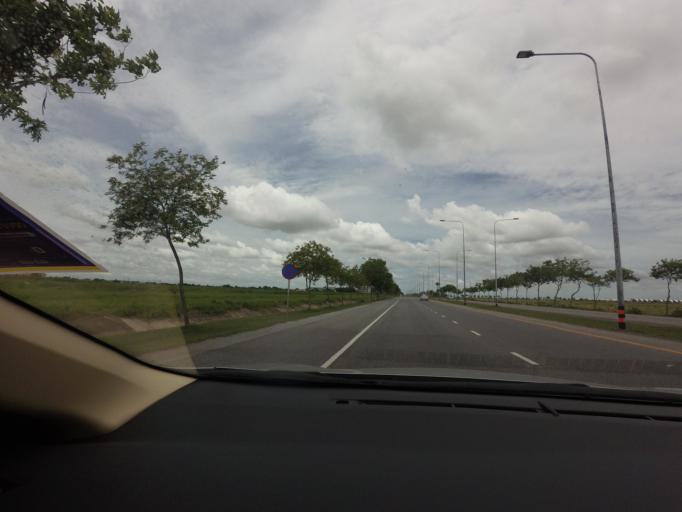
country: TH
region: Bangkok
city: Lat Krabang
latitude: 13.7046
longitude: 100.7738
